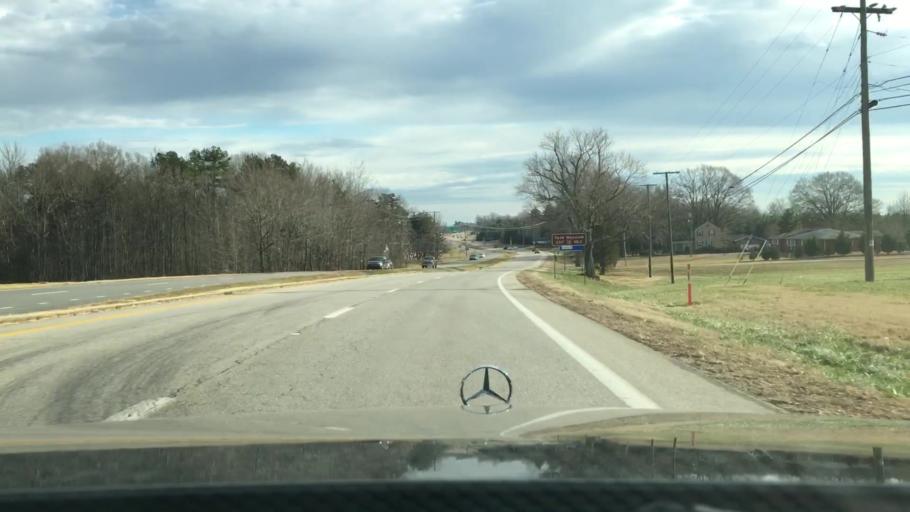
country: US
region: Virginia
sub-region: Pittsylvania County
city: Mount Hermon
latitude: 36.7110
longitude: -79.3755
